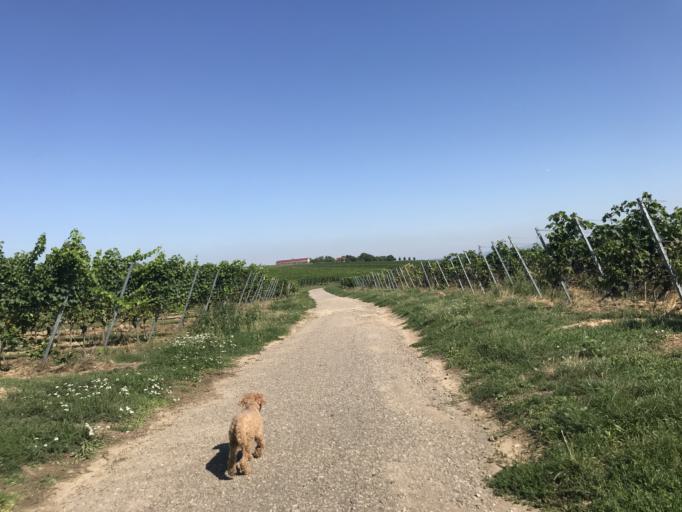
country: DE
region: Rheinland-Pfalz
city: Bodenheim
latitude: 49.9542
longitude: 8.3015
